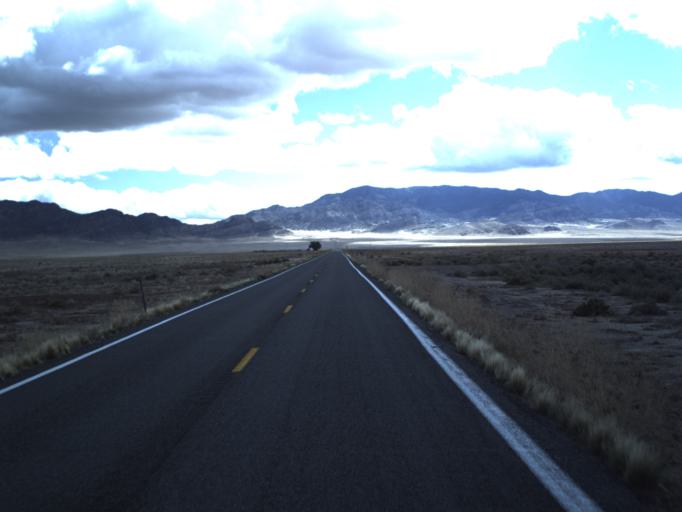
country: US
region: Utah
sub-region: Beaver County
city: Milford
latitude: 38.5402
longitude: -113.7033
